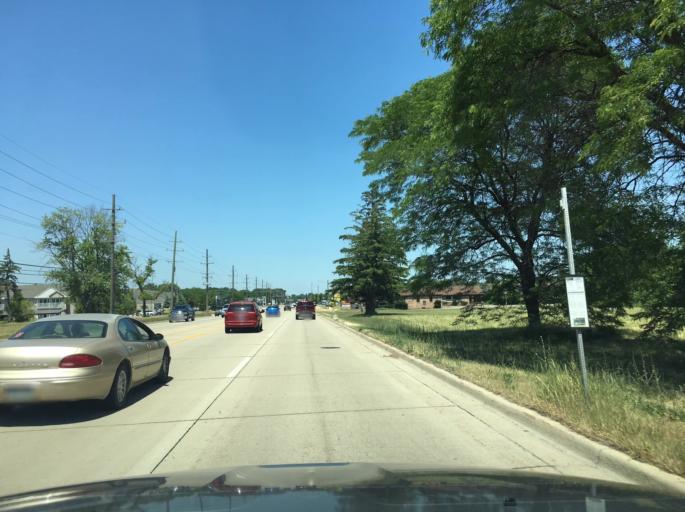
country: US
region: Michigan
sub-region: Macomb County
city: Fraser
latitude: 42.5611
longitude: -82.9506
